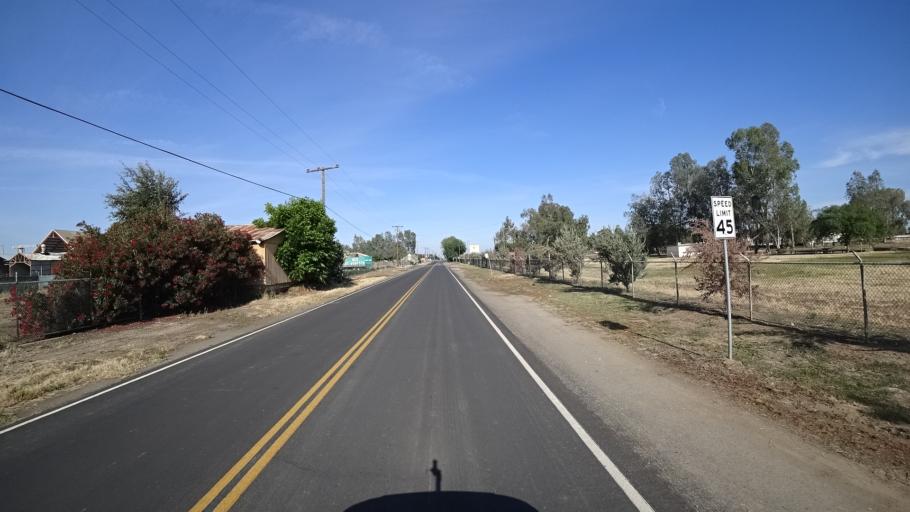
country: US
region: California
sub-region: Kings County
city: Home Garden
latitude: 36.3134
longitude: -119.6326
